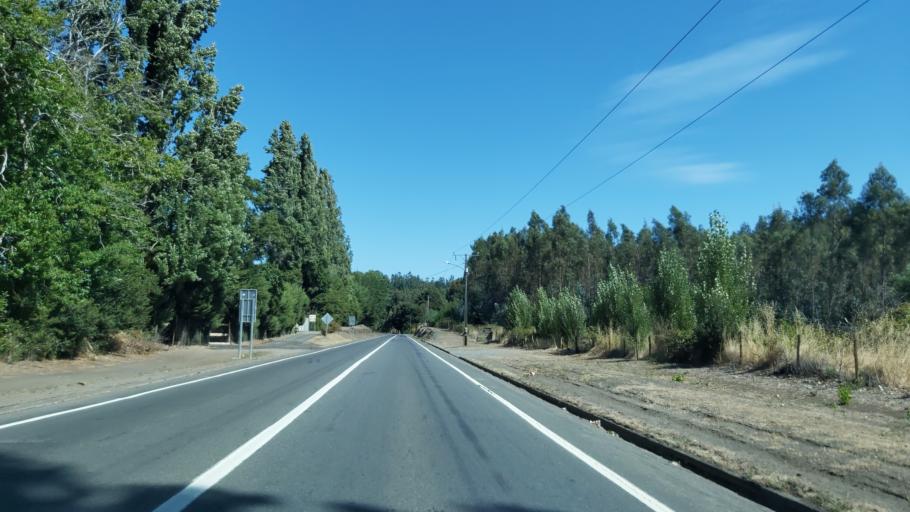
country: CL
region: Biobio
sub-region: Provincia de Concepcion
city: Coronel
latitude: -37.1086
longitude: -72.9883
